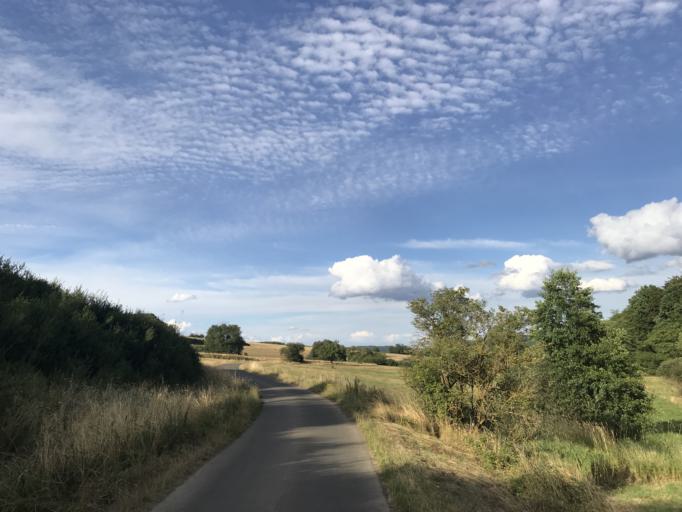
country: DE
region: Hesse
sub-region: Regierungsbezirk Giessen
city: Lohra
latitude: 50.6780
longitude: 8.5830
